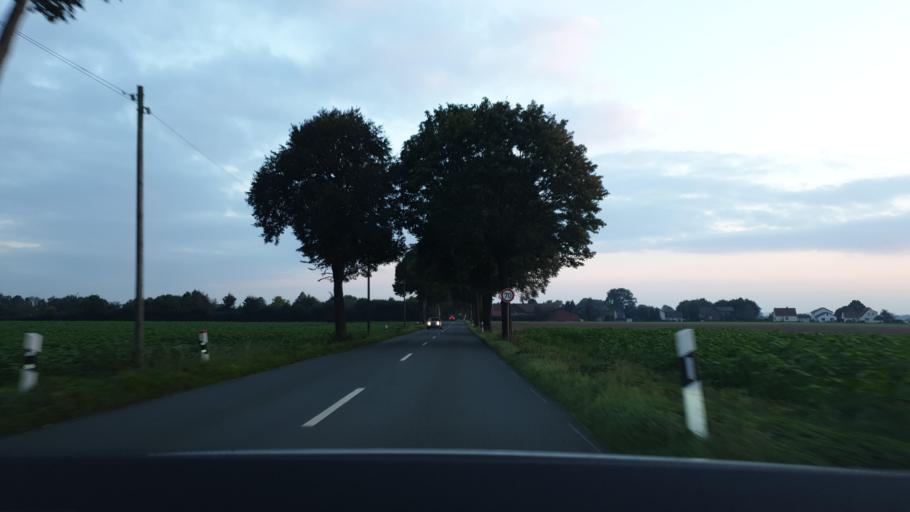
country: DE
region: North Rhine-Westphalia
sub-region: Regierungsbezirk Detmold
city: Hille
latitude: 52.2576
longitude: 8.7426
